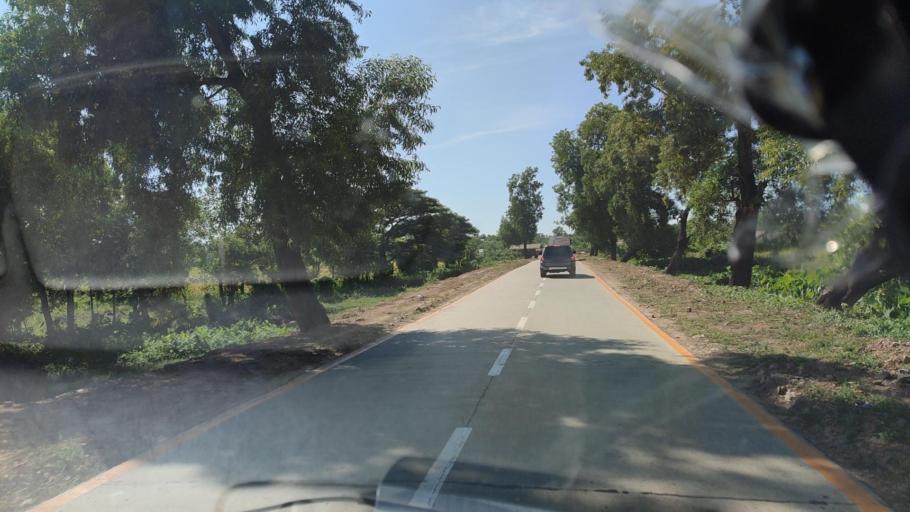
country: MM
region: Rakhine
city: Sittwe
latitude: 20.4779
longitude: 93.2721
